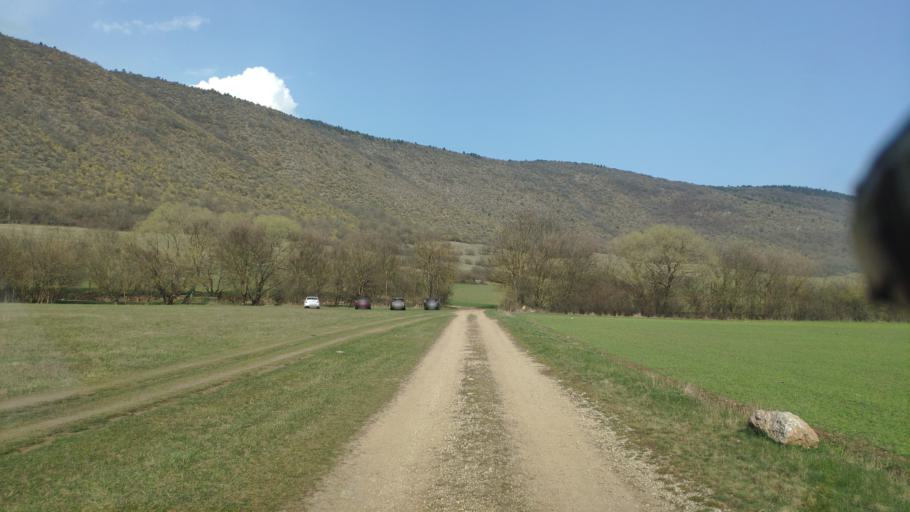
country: SK
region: Kosicky
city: Medzev
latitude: 48.6216
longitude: 20.8908
